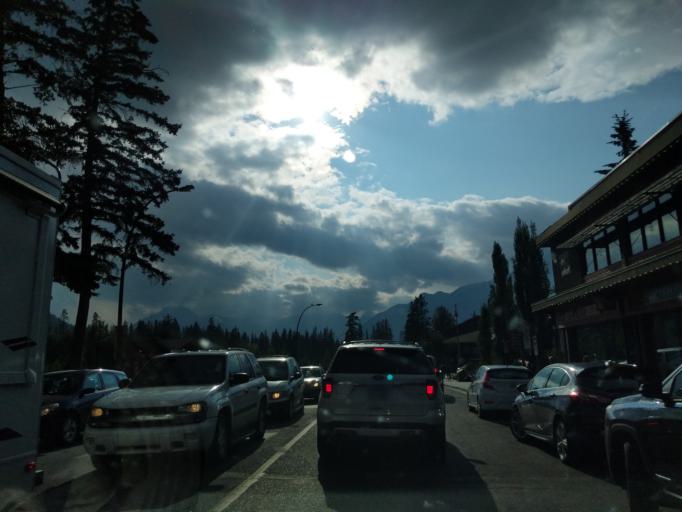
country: CA
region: Alberta
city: Banff
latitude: 51.1744
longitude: -115.5716
